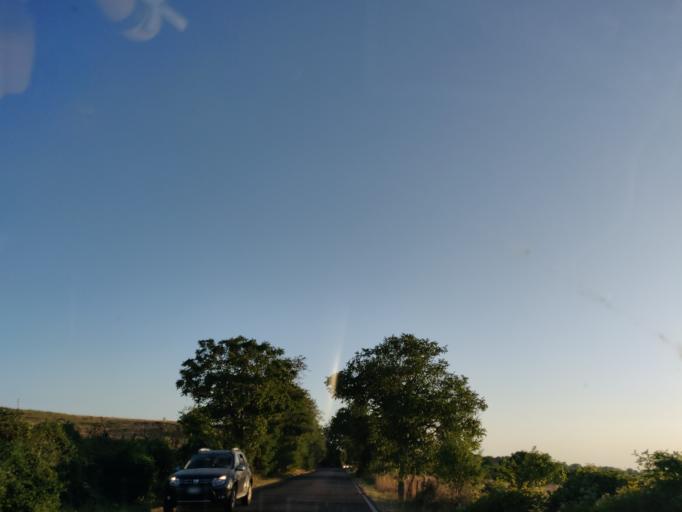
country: IT
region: Latium
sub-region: Provincia di Viterbo
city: Canino
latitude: 42.4106
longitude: 11.6986
